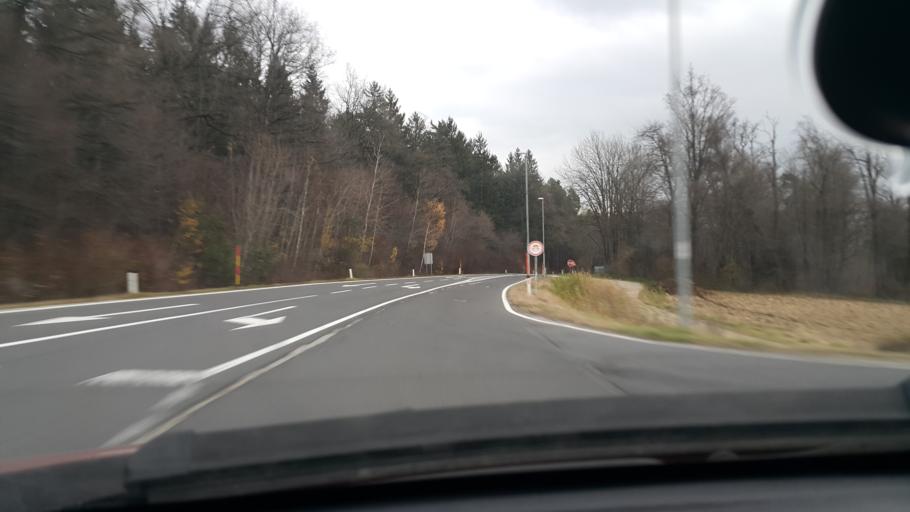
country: SI
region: Slovenska Bistrica
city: Zgornja Polskava
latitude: 46.3989
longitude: 15.6059
